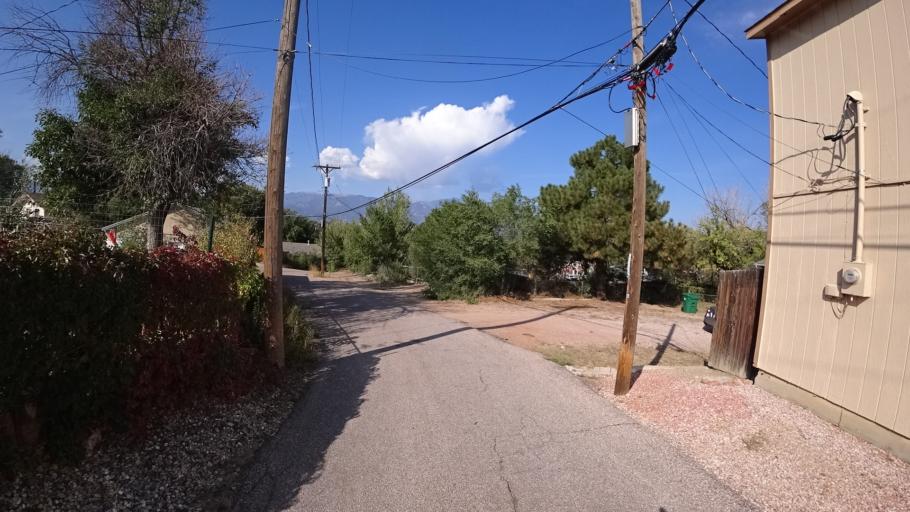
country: US
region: Colorado
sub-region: El Paso County
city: Colorado Springs
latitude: 38.8540
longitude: -104.7747
